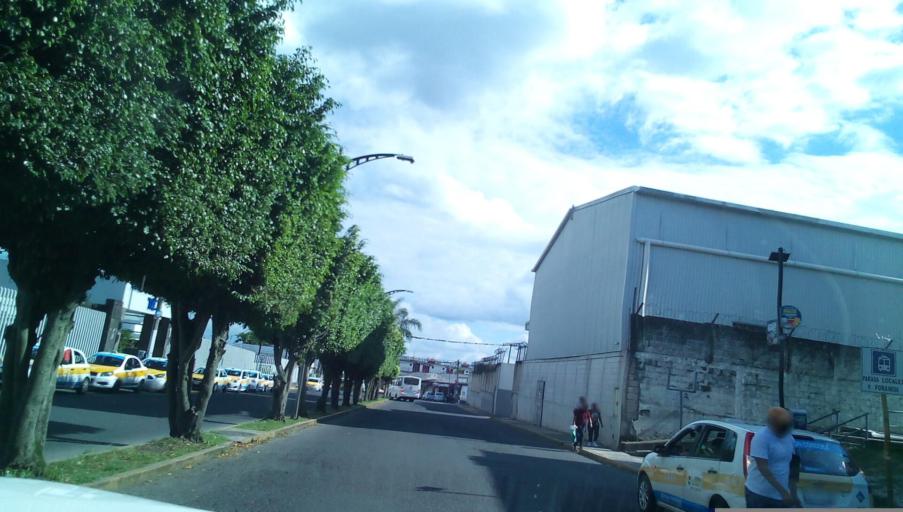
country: MX
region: Veracruz
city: Cordoba
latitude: 18.8837
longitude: -96.9211
